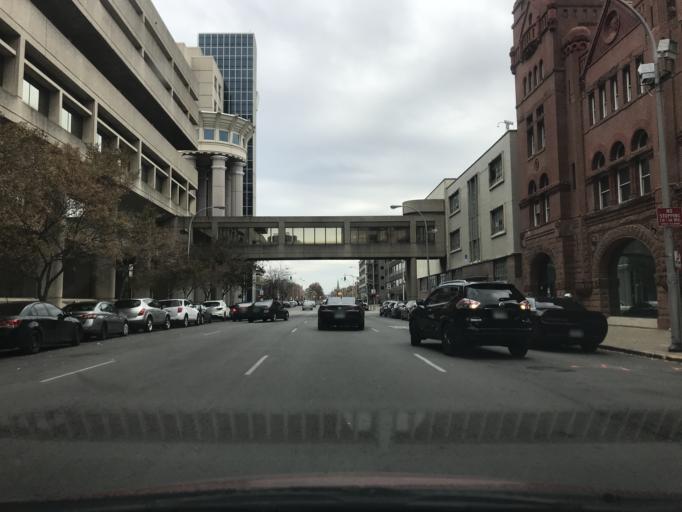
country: US
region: Kentucky
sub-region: Jefferson County
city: Louisville
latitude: 38.2543
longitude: -85.7610
